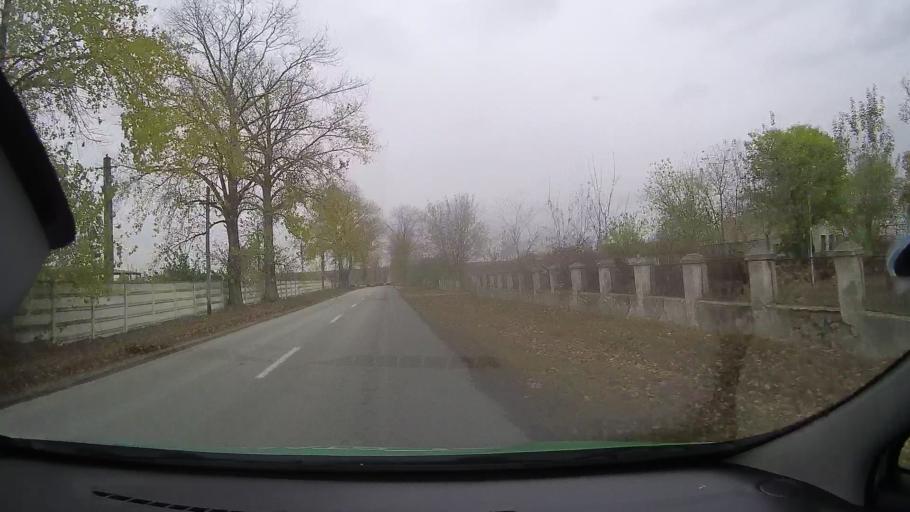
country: RO
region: Constanta
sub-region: Comuna Pantelimon
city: Pantelimon
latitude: 44.5502
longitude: 28.3288
